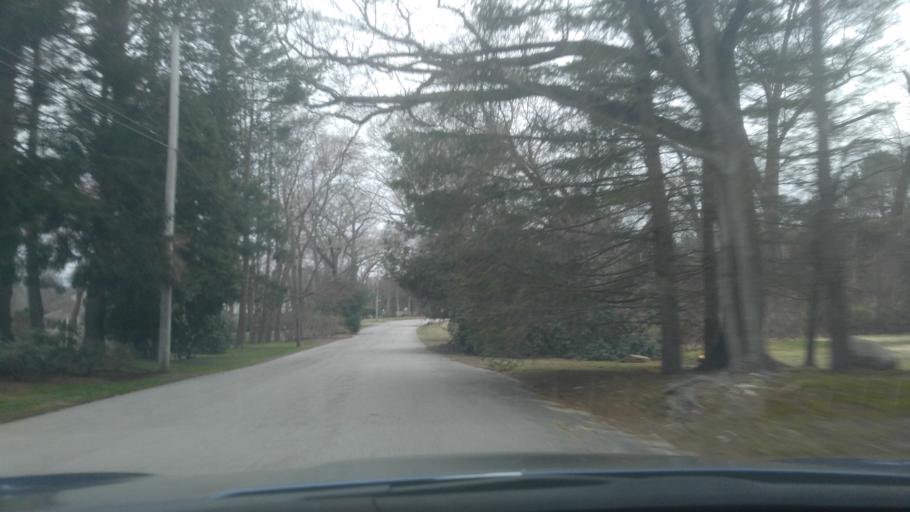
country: US
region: Rhode Island
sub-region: Kent County
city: East Greenwich
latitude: 41.6675
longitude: -71.4604
